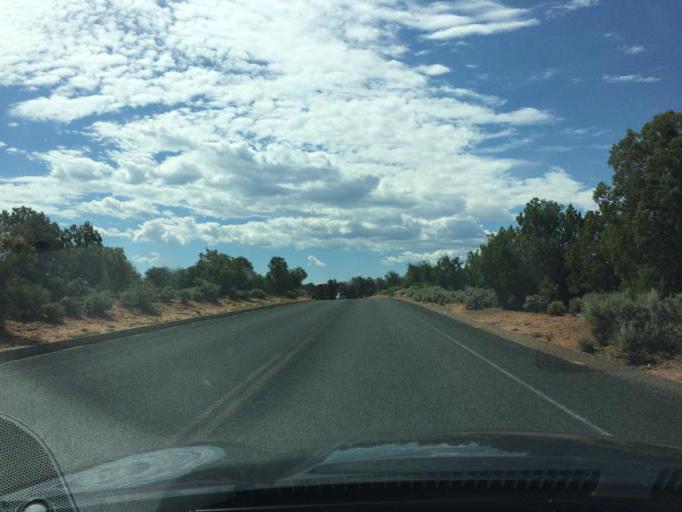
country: US
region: Arizona
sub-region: Apache County
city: Chinle
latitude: 36.1015
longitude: -109.3656
